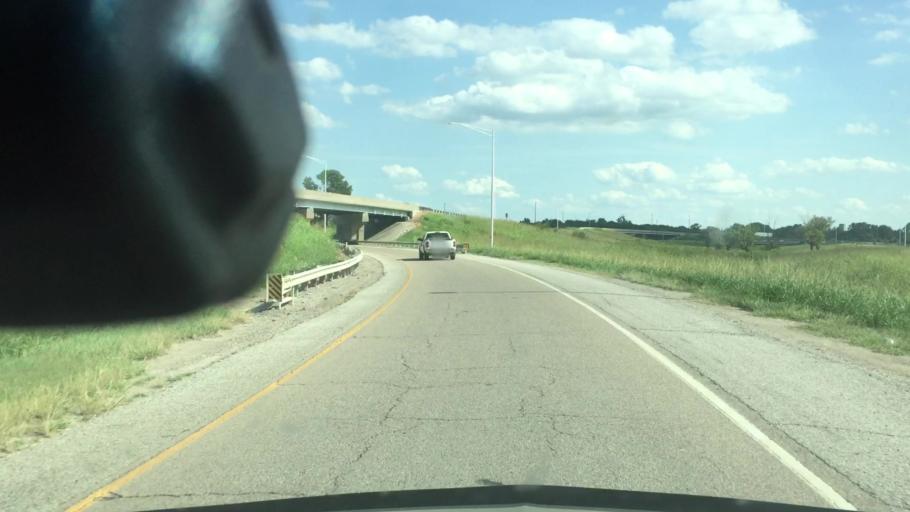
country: US
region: Illinois
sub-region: Saint Clair County
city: East Saint Louis
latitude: 38.6487
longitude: -90.1325
